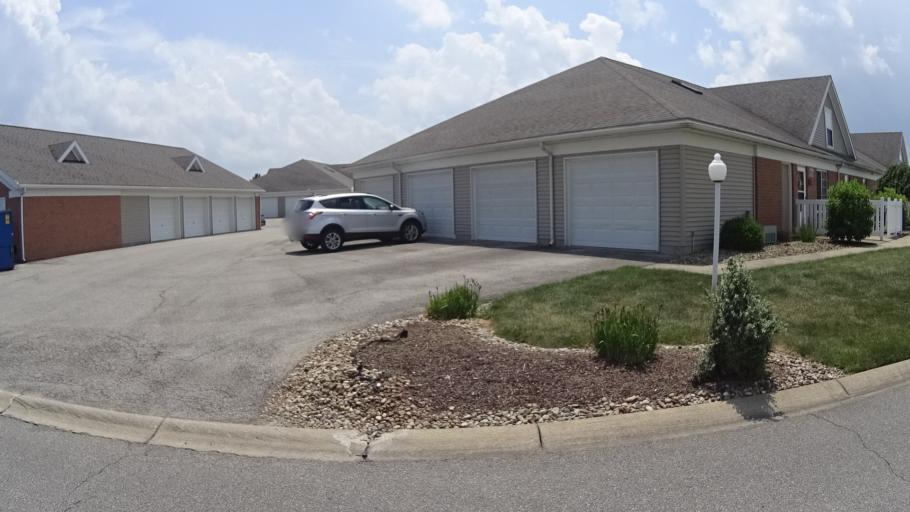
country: US
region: Ohio
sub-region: Lorain County
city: Vermilion
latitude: 41.4084
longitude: -82.3697
